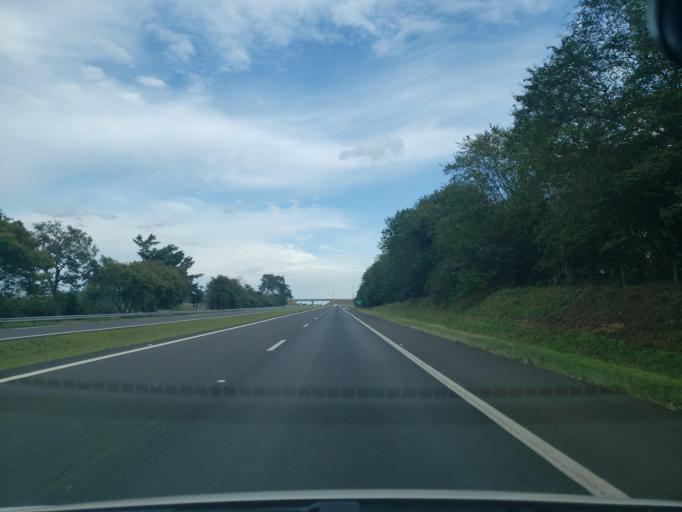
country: BR
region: Sao Paulo
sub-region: Itirapina
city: Itirapina
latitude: -22.2672
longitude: -47.9289
